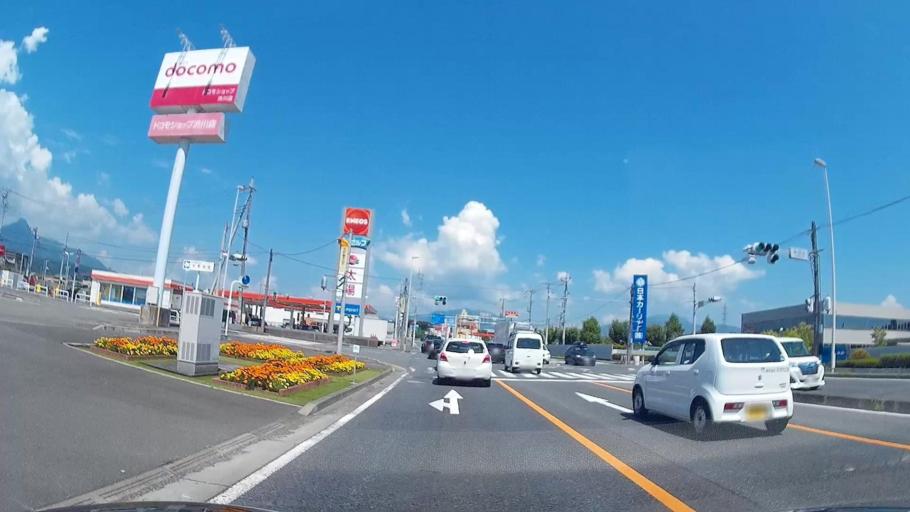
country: JP
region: Gunma
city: Shibukawa
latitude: 36.4741
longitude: 139.0227
